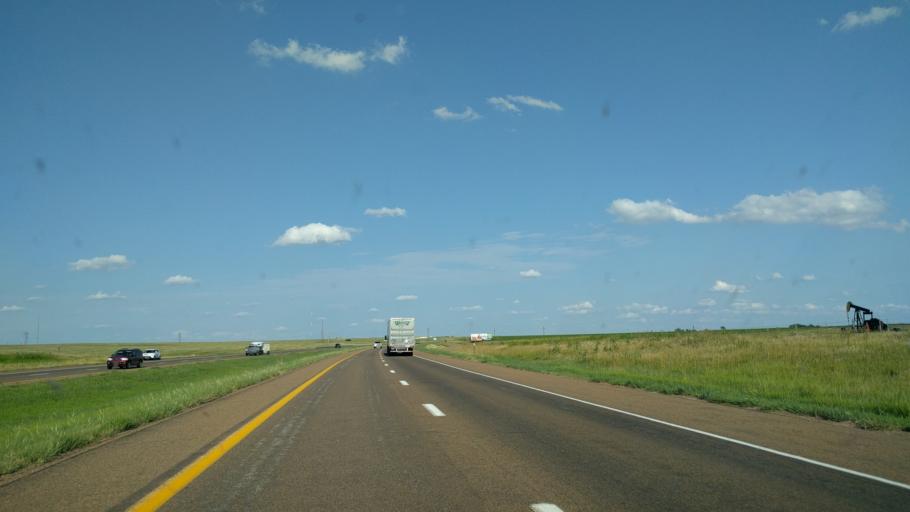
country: US
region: Kansas
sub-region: Ellis County
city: Hays
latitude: 38.9216
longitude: -99.3869
